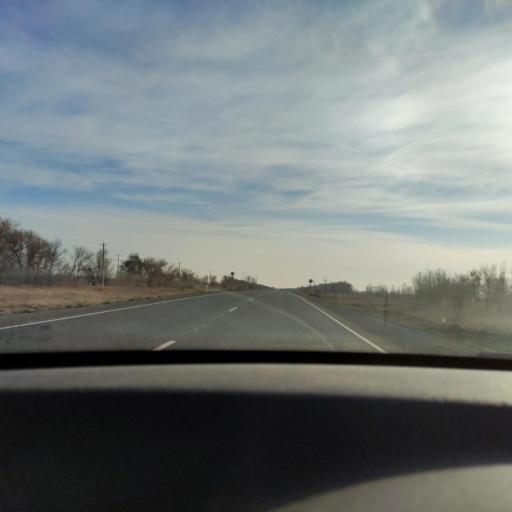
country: RU
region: Samara
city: Krasnoarmeyskoye
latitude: 52.8113
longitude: 50.0117
